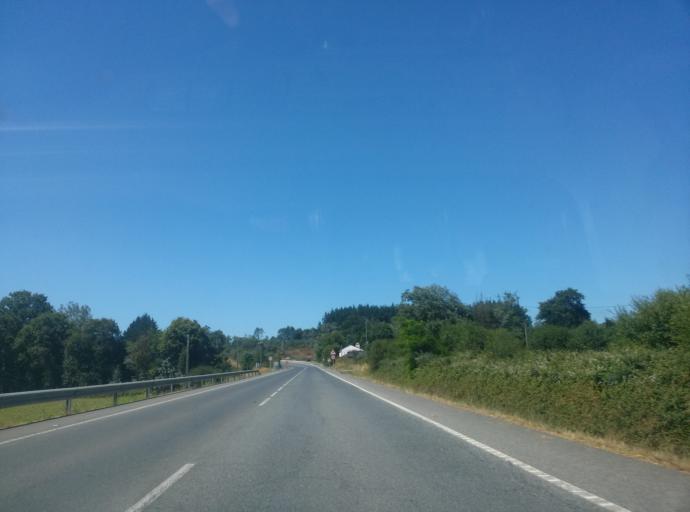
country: ES
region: Galicia
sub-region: Provincia de Lugo
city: Mos
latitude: 43.1227
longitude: -7.4857
